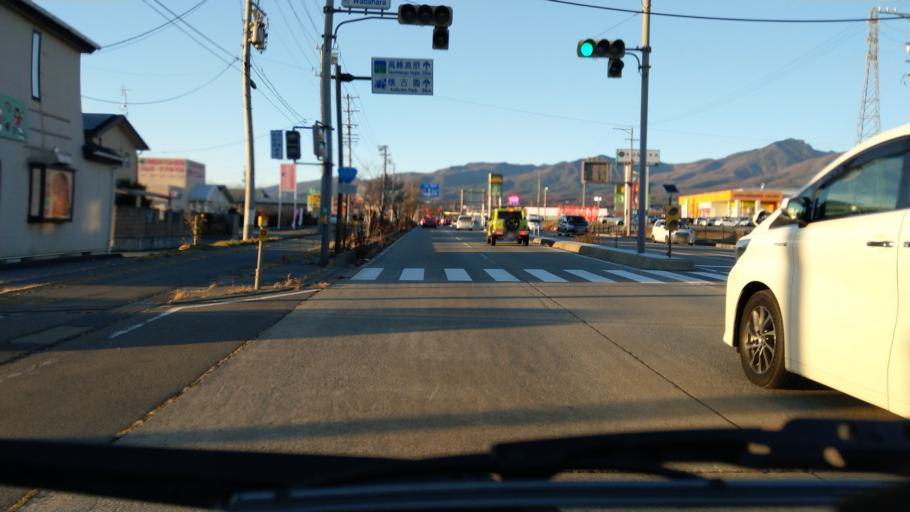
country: JP
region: Nagano
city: Komoro
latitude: 36.2955
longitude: 138.4691
